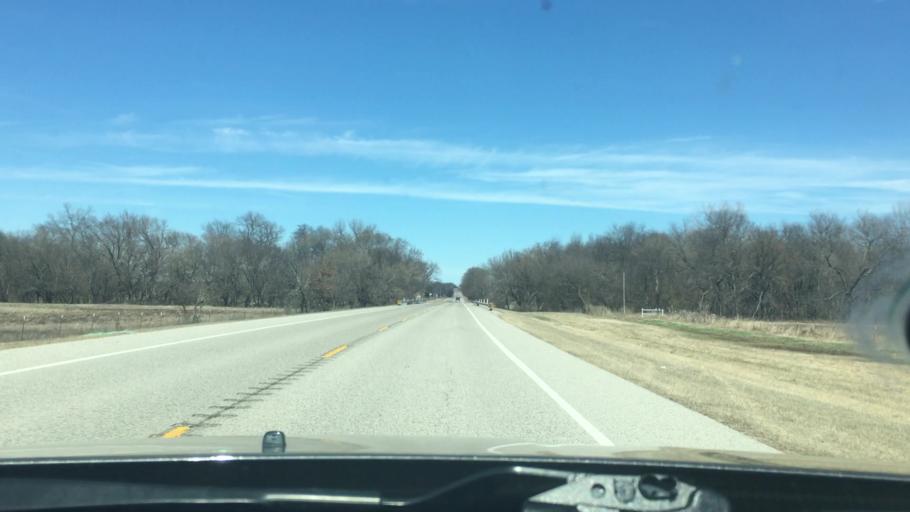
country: US
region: Oklahoma
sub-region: Murray County
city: Sulphur
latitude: 34.3885
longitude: -96.9511
